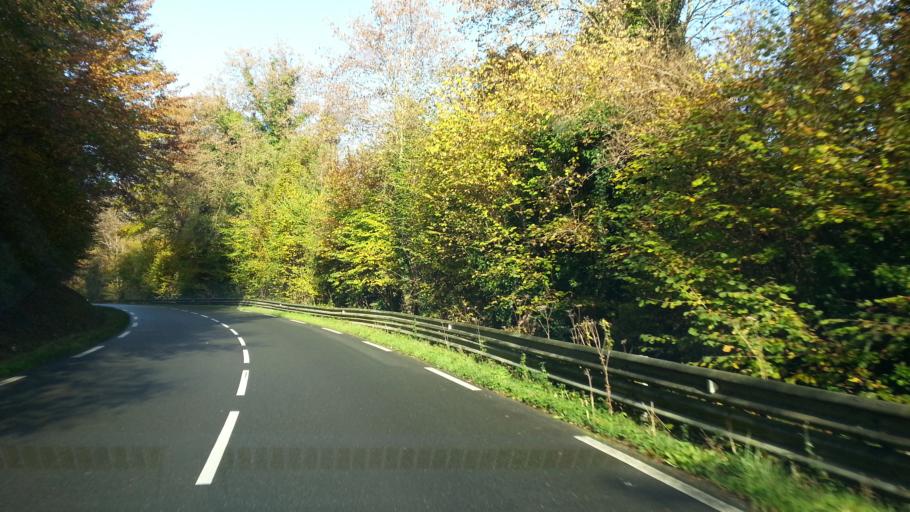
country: FR
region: Picardie
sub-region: Departement de l'Oise
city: Cires-les-Mello
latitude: 49.2844
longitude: 2.3610
